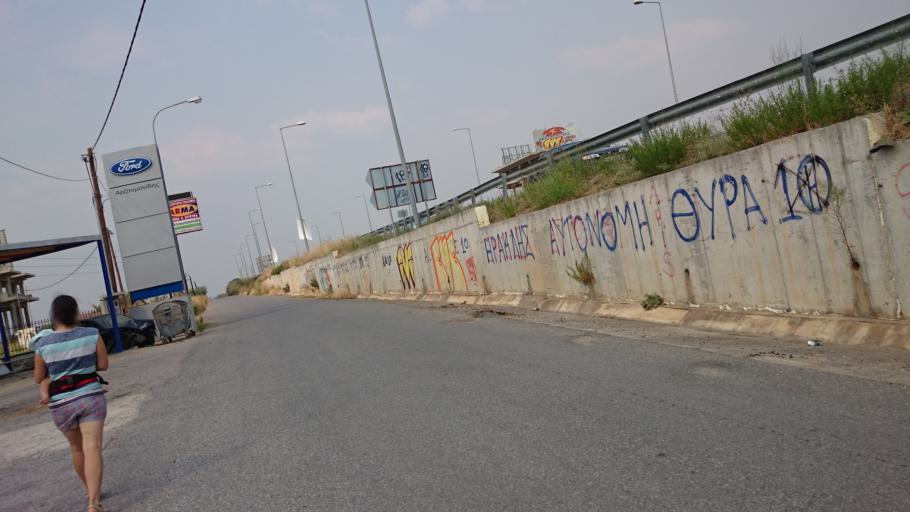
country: GR
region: Central Macedonia
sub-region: Nomos Chalkidikis
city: Nea Moudhania
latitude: 40.2606
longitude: 23.2735
